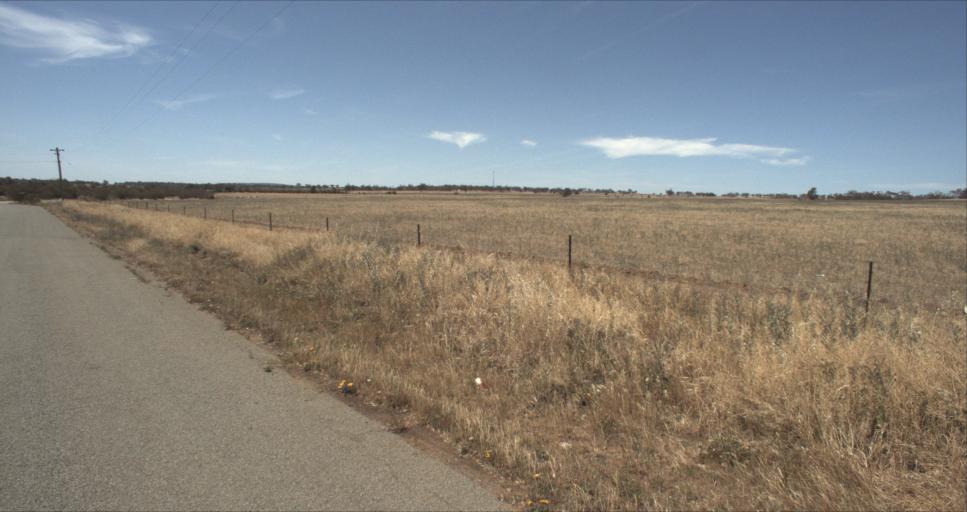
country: AU
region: New South Wales
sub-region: Leeton
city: Leeton
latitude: -34.6080
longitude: 146.4351
